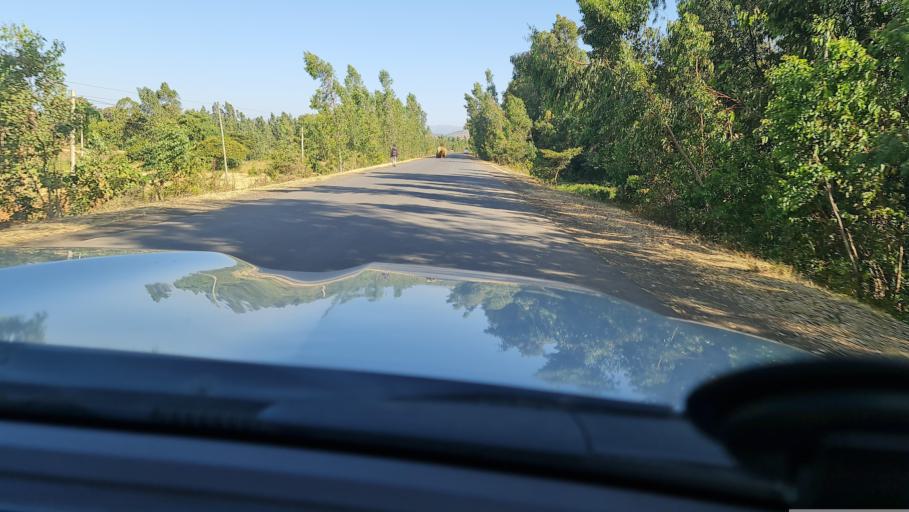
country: ET
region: Oromiya
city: Waliso
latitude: 8.5756
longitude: 37.9418
